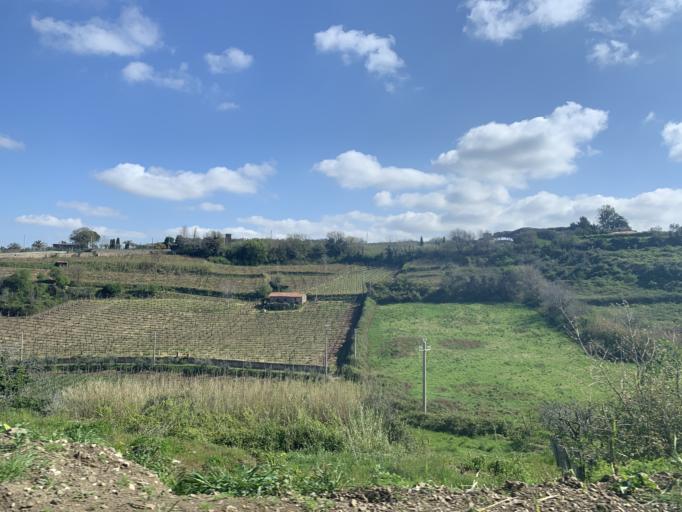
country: IT
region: Latium
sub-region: Citta metropolitana di Roma Capitale
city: Grottaferrata
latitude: 41.7832
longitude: 12.6517
